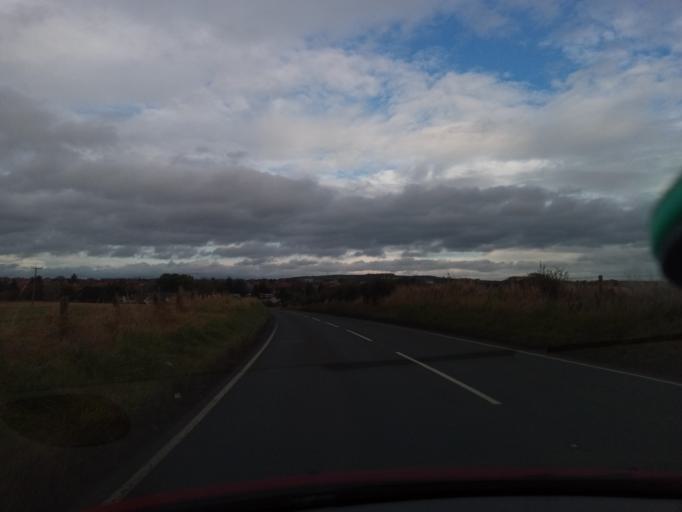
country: GB
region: Scotland
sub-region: West Lothian
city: Blackburn
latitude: 55.8681
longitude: -3.6236
